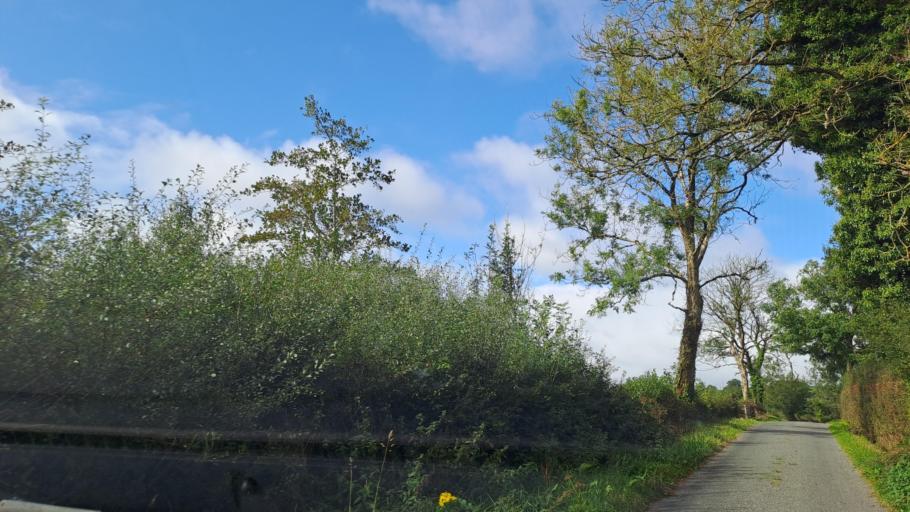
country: IE
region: Ulster
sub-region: An Cabhan
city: Kingscourt
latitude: 53.9703
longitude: -6.8592
